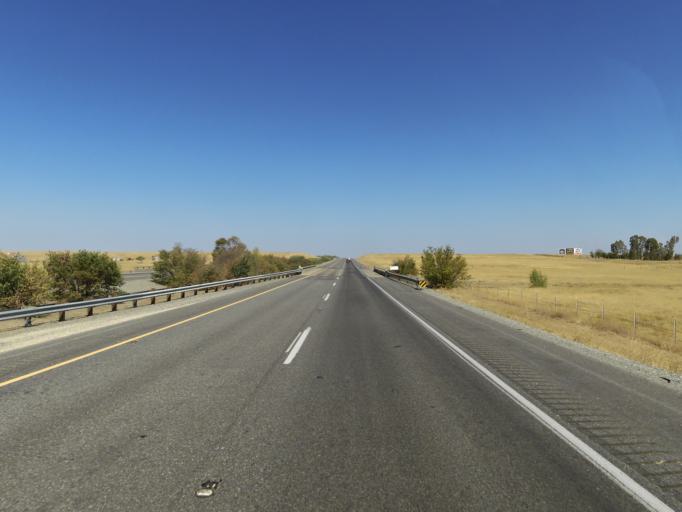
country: US
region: California
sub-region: Glenn County
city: Orland
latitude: 39.8142
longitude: -122.1998
